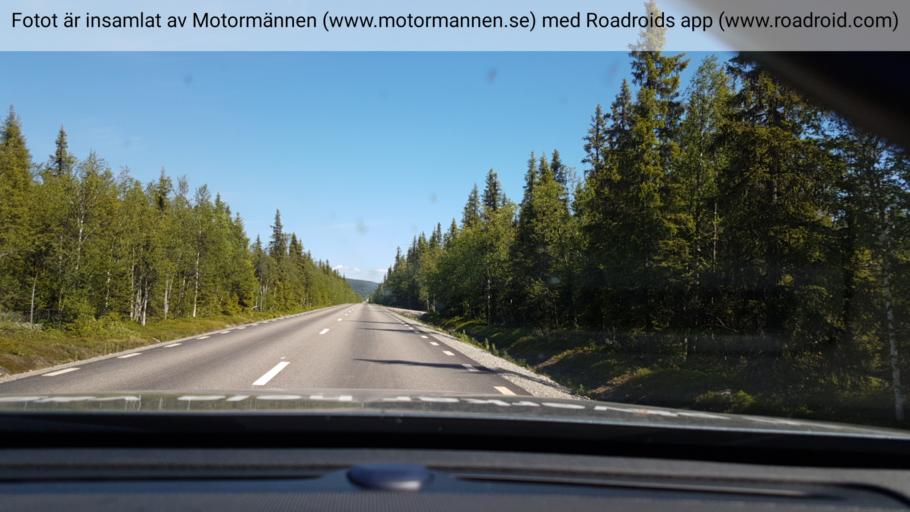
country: SE
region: Vaesterbotten
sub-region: Asele Kommun
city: Insjon
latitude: 64.7266
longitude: 17.5744
